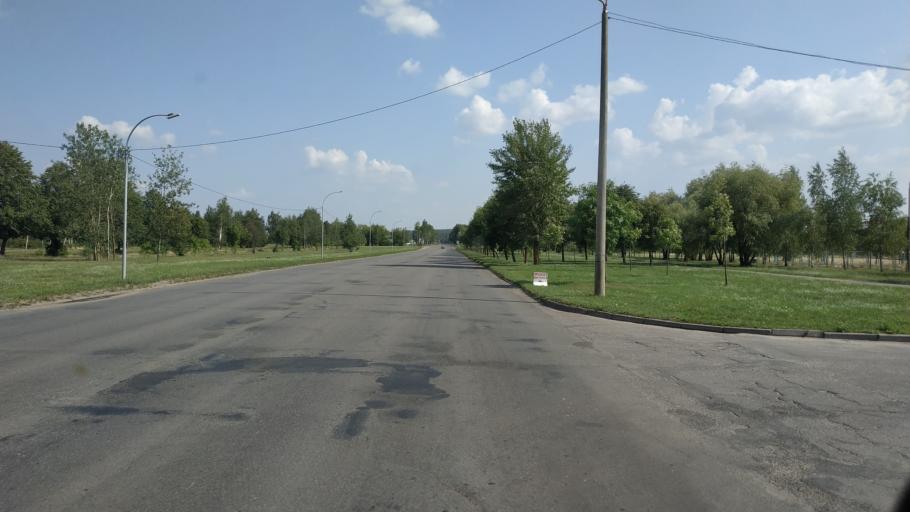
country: BY
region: Mogilev
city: Buynichy
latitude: 53.8600
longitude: 30.3250
